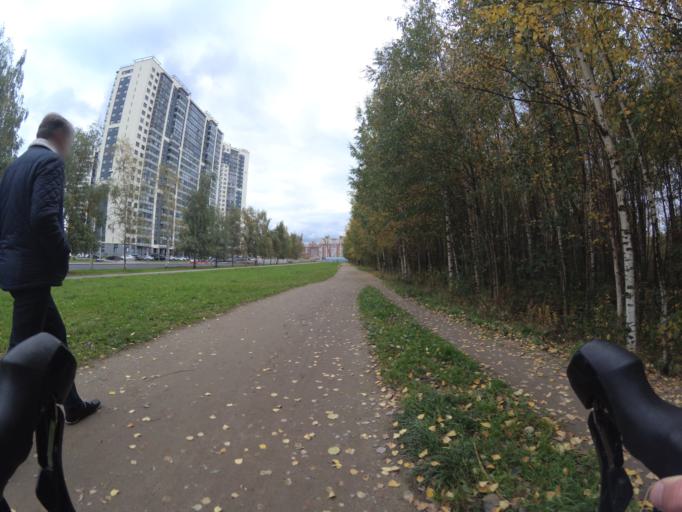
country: RU
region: Leningrad
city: Untolovo
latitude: 59.9956
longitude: 30.1920
